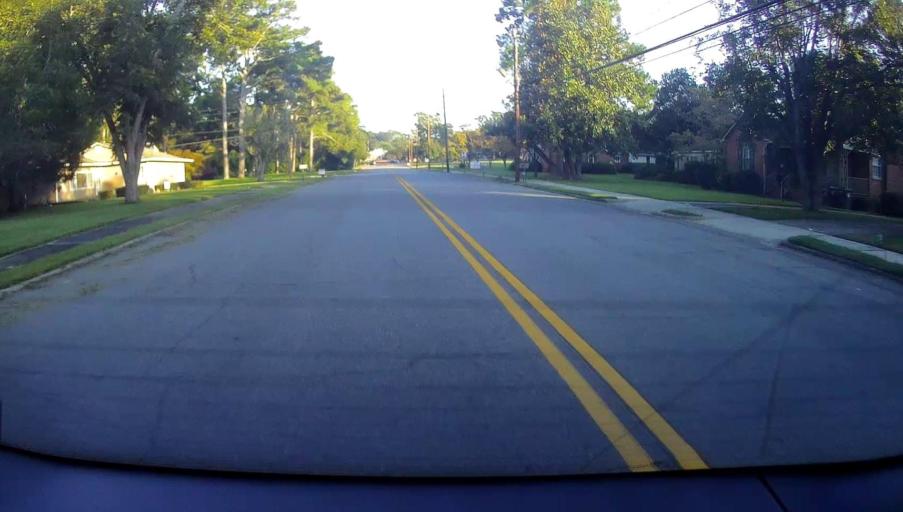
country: US
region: Georgia
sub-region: Bleckley County
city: Cochran
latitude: 32.3831
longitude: -83.3485
